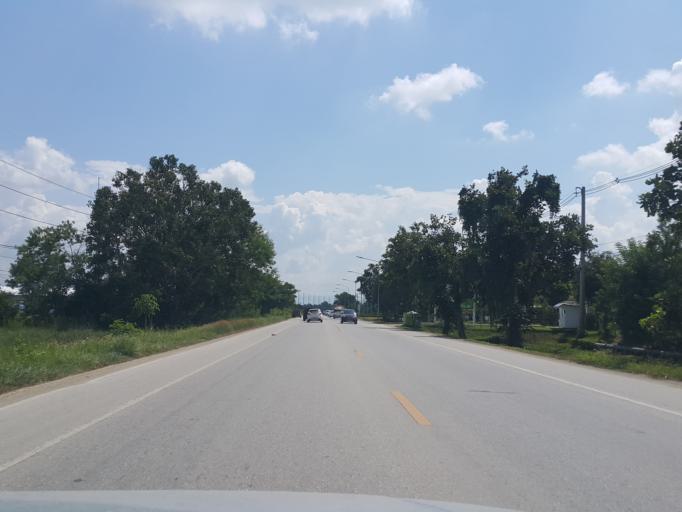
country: TH
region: Chiang Mai
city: San Sai
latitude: 18.7992
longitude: 99.0642
